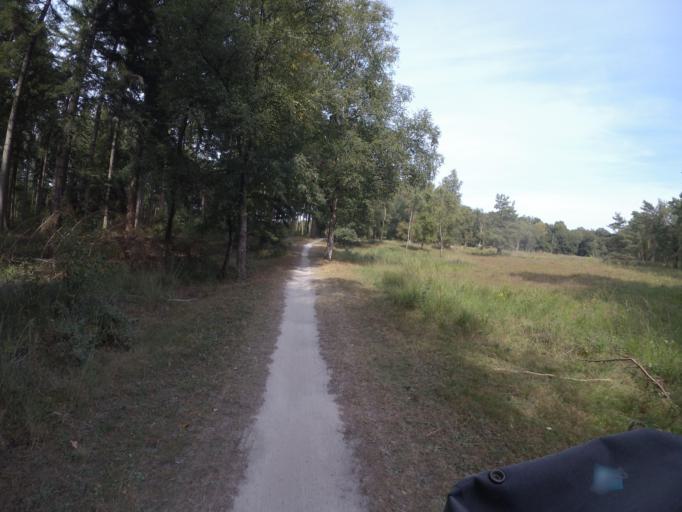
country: NL
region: Drenthe
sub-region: Gemeente Westerveld
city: Havelte
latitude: 52.8139
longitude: 6.2645
